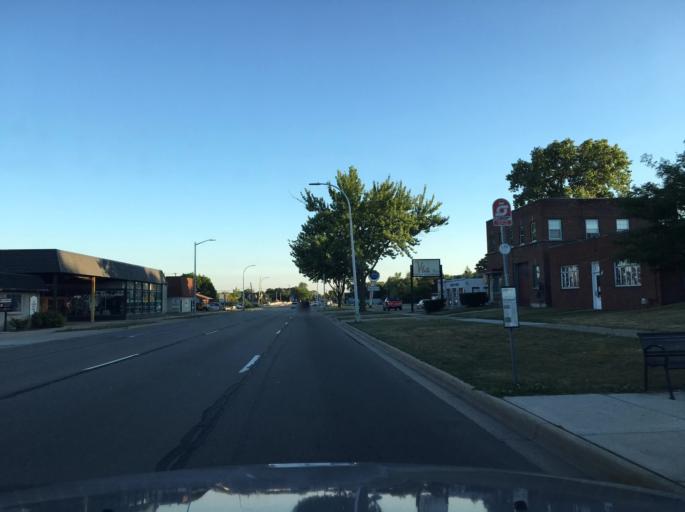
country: US
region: Michigan
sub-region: Macomb County
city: Mount Clemens
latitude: 42.5873
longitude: -82.8826
